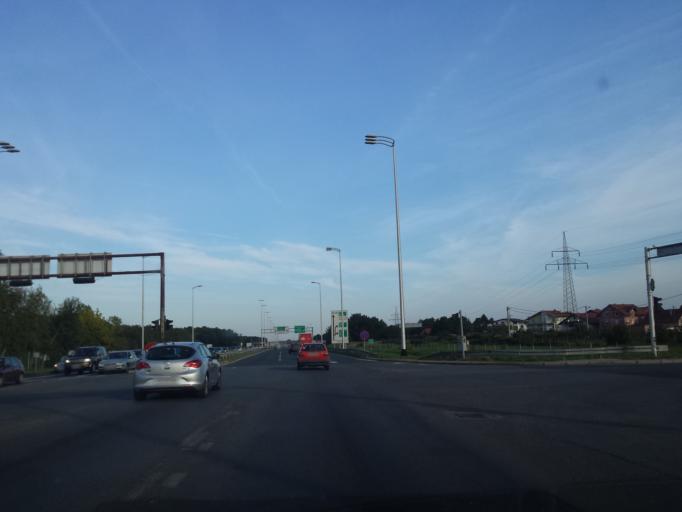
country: HR
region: Grad Zagreb
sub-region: Sesvete
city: Sesvete
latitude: 45.8028
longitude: 16.1186
